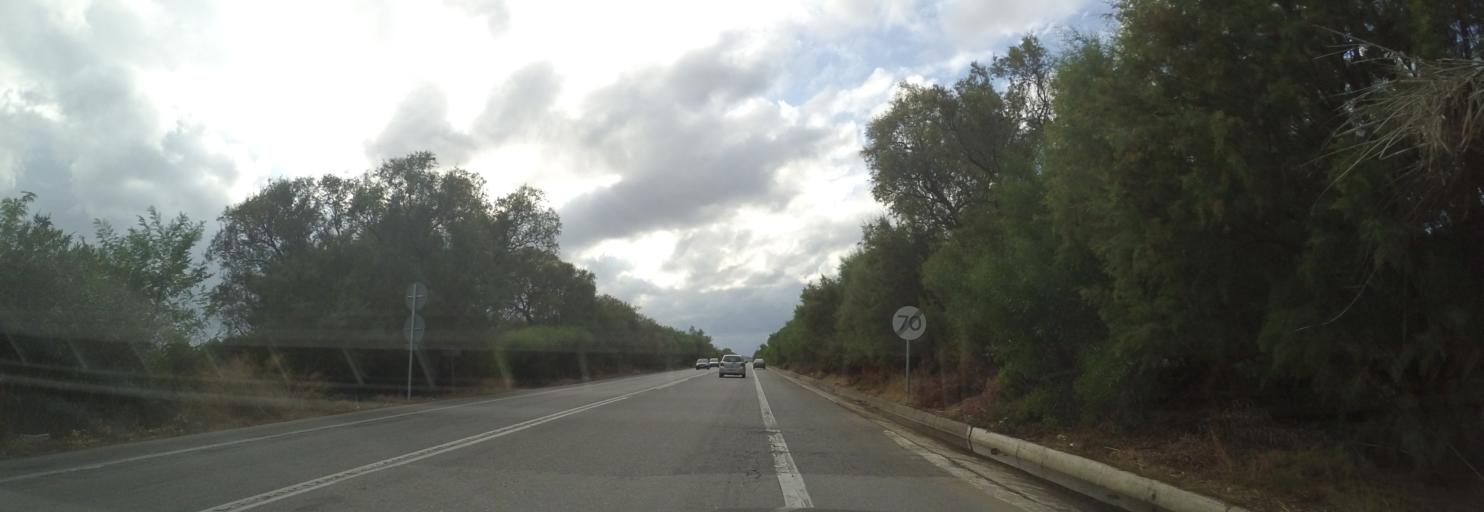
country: GR
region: Crete
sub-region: Nomos Rethymnis
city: Panormos
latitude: 35.4139
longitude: 24.7174
